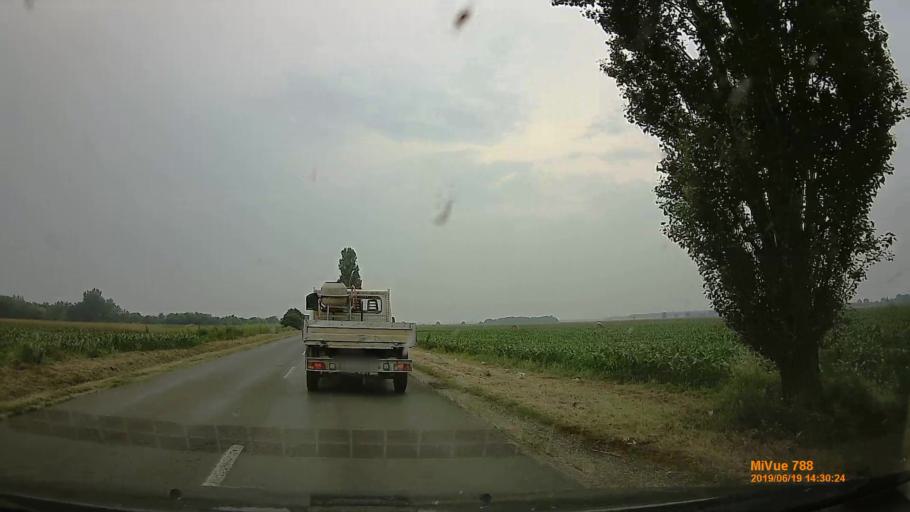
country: HU
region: Baranya
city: Szigetvar
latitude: 46.0621
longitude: 17.7742
